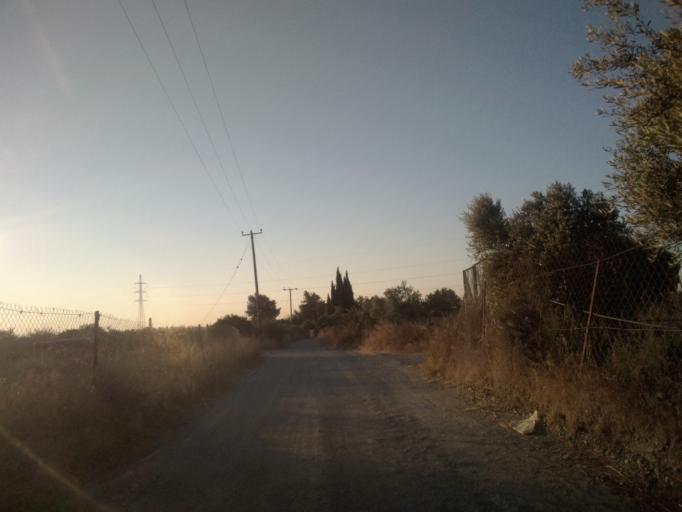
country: CY
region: Limassol
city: Ypsonas
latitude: 34.6687
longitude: 32.9670
